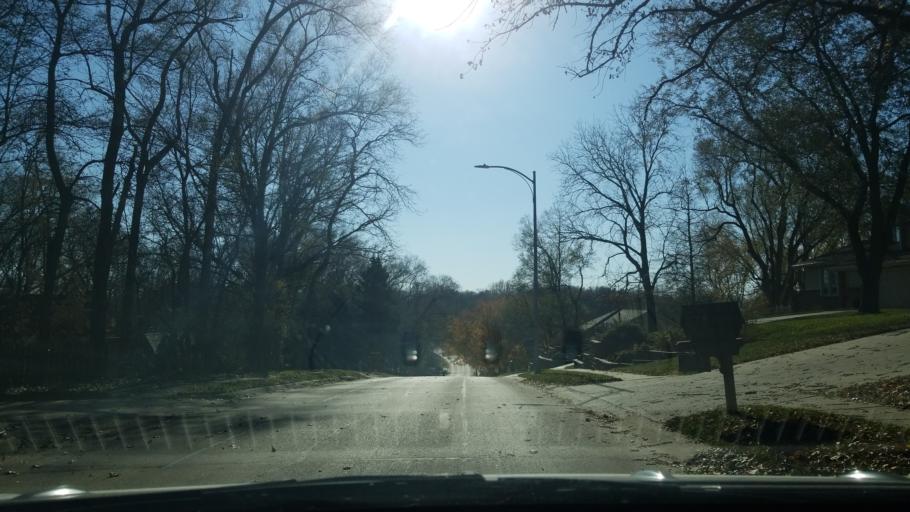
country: US
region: Nebraska
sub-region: Sarpy County
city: Bellevue
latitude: 41.1634
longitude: -95.9006
